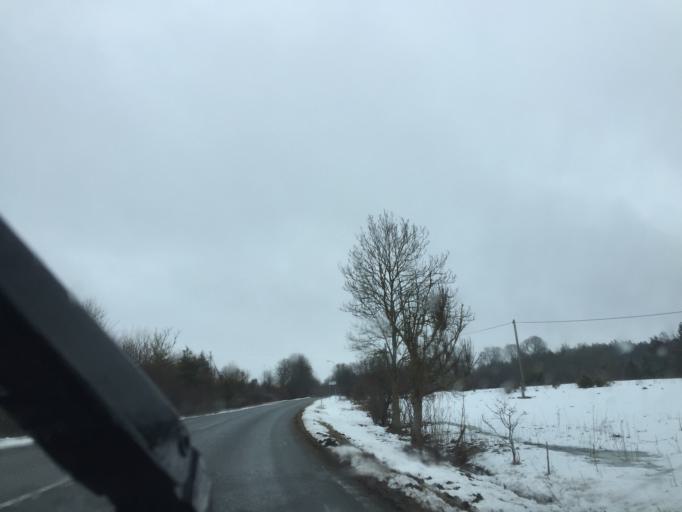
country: EE
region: Saare
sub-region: Kuressaare linn
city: Kuressaare
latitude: 58.3547
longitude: 22.0332
